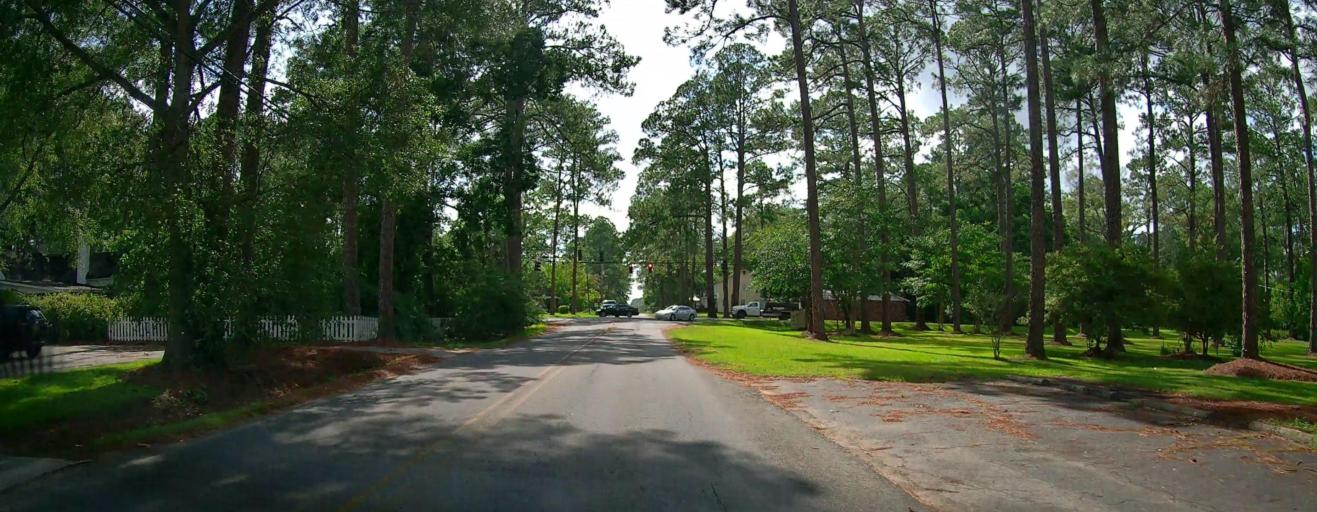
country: US
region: Georgia
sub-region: Coffee County
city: Douglas
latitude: 31.5170
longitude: -82.8438
